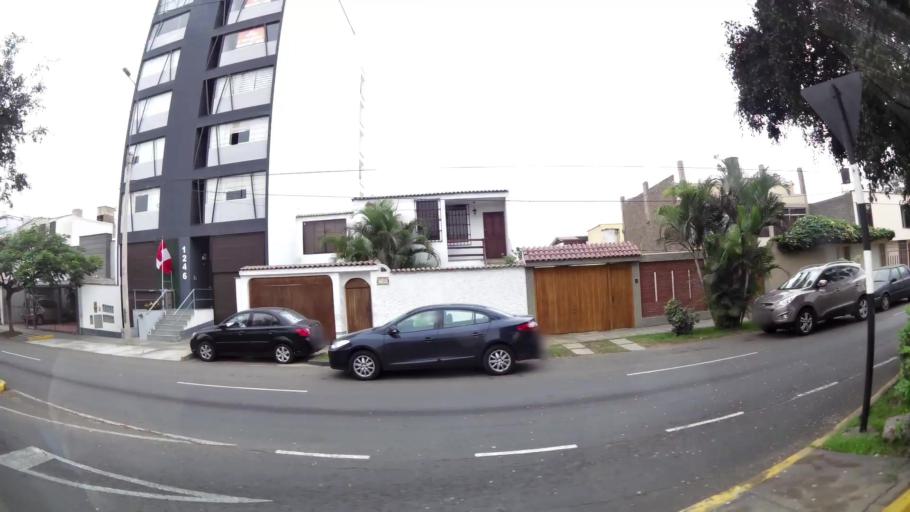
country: PE
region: Lima
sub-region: Lima
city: Surco
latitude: -12.1159
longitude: -77.0100
